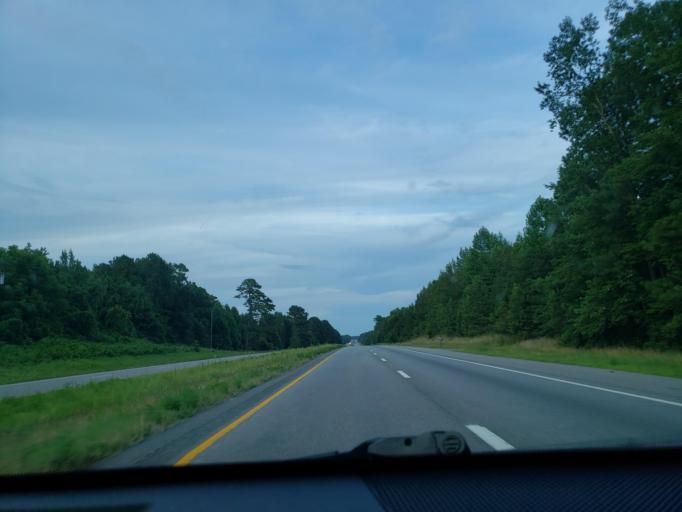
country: US
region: Virginia
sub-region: City of Emporia
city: Emporia
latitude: 36.6963
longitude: -77.3391
